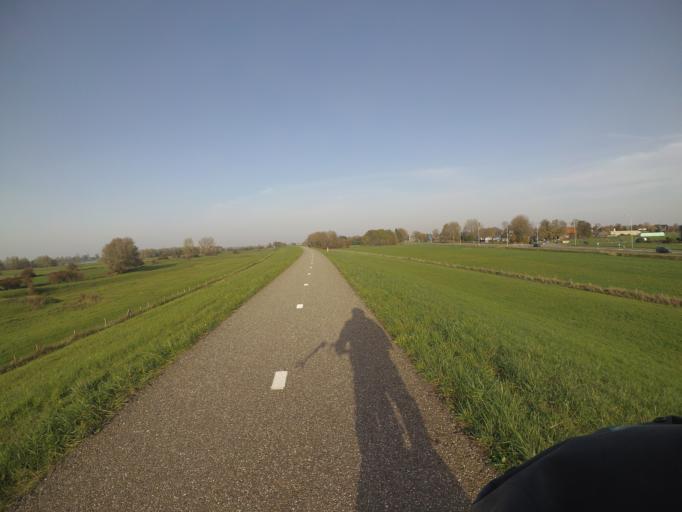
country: NL
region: Gelderland
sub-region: Gemeente Maasdriel
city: Heerewaarden
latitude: 51.8144
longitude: 5.3833
